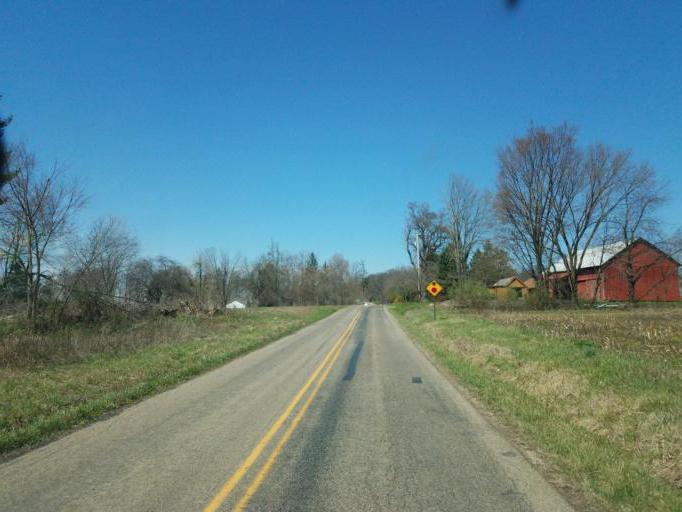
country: US
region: Ohio
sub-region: Knox County
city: Gambier
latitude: 40.3211
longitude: -82.3081
